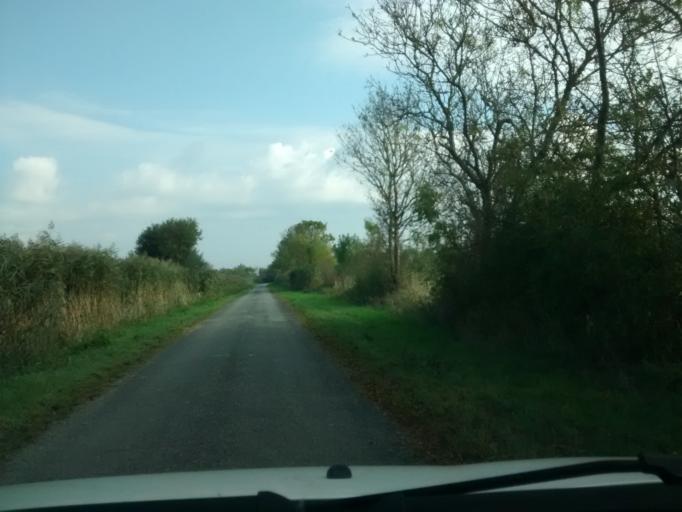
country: FR
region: Pays de la Loire
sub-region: Departement de la Loire-Atlantique
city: Cordemais
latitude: 47.2460
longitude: -1.8655
